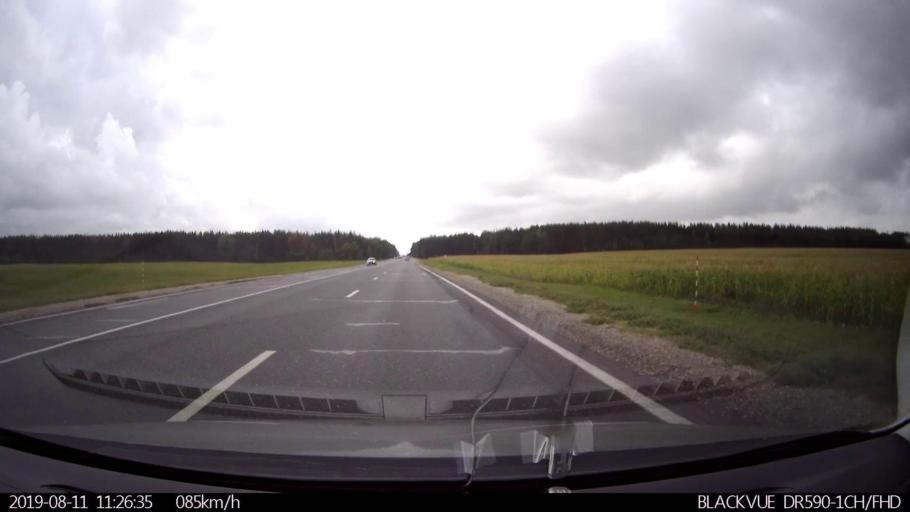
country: RU
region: Ulyanovsk
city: Krasnyy Gulyay
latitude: 54.1035
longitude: 48.2346
